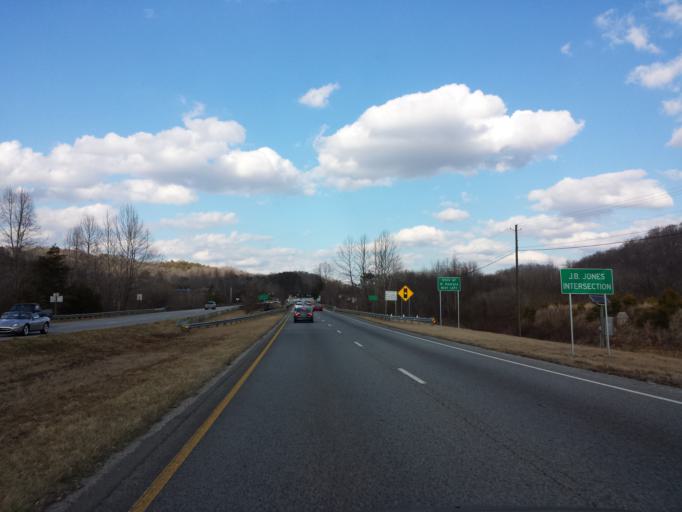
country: US
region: Georgia
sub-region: Lumpkin County
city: Dahlonega
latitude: 34.4655
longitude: -83.9695
